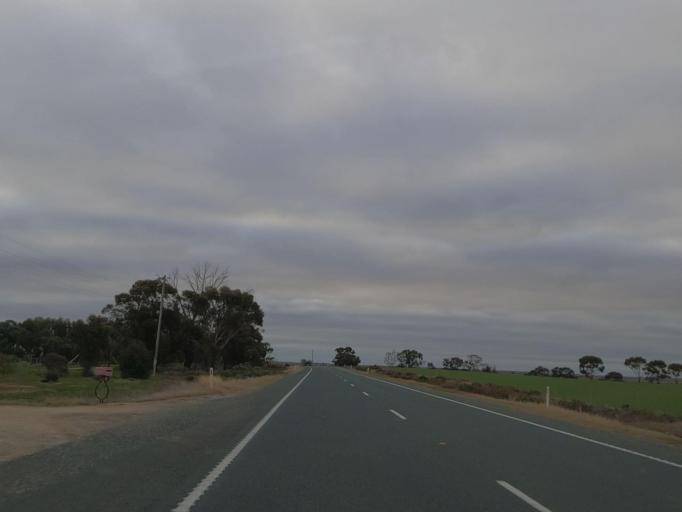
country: AU
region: Victoria
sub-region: Swan Hill
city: Swan Hill
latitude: -35.5574
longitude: 143.7785
